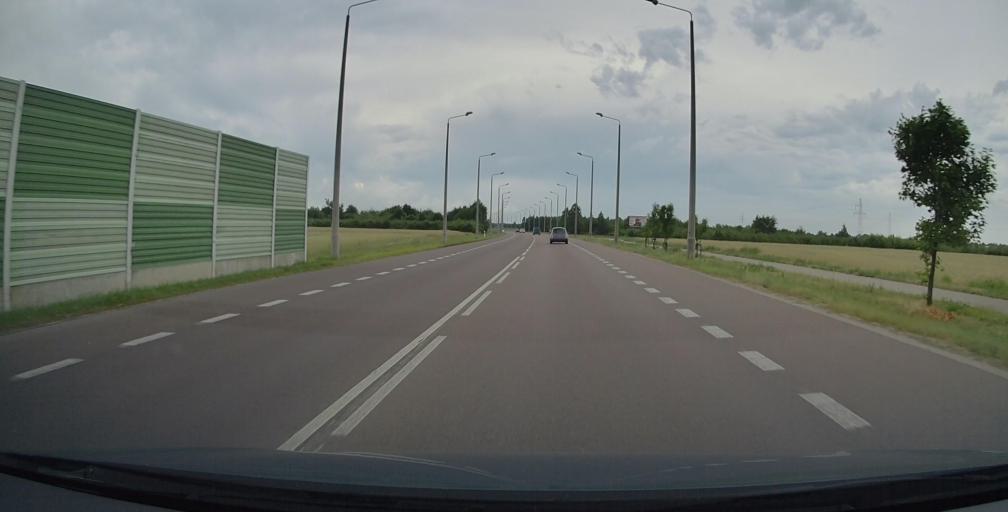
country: PL
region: Lublin Voivodeship
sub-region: Biala Podlaska
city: Biala Podlaska
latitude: 52.0514
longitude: 23.1363
